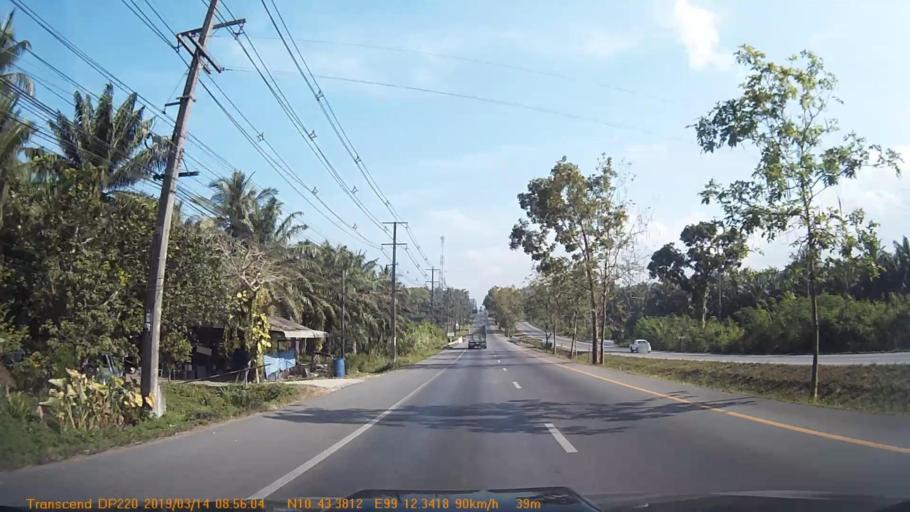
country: TH
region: Chumphon
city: Tha Sae
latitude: 10.7235
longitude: 99.2057
